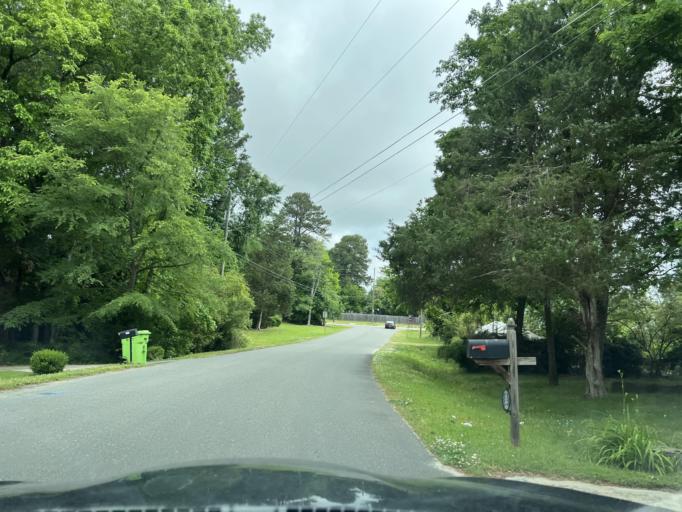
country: US
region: North Carolina
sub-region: Wake County
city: Rolesville
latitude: 35.8700
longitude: -78.5493
